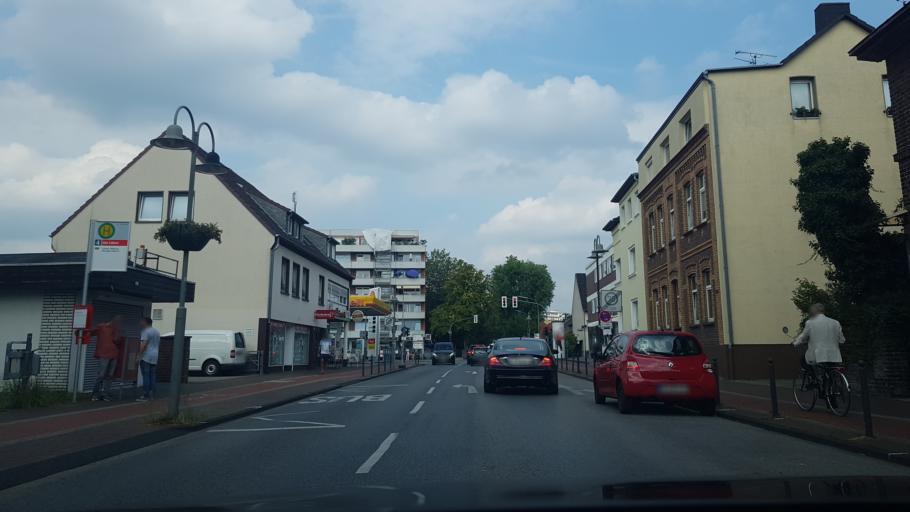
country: DE
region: North Rhine-Westphalia
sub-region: Regierungsbezirk Dusseldorf
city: Ratingen
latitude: 51.3363
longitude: 6.8344
